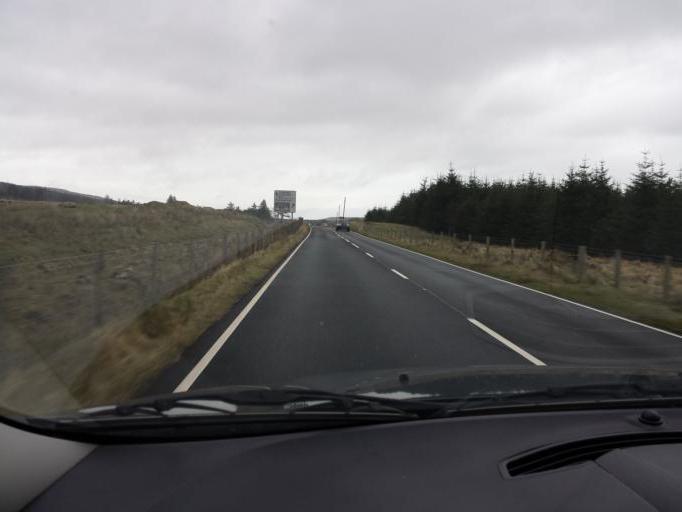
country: GB
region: Northern Ireland
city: Glenariff
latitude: 55.0111
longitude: -6.1485
